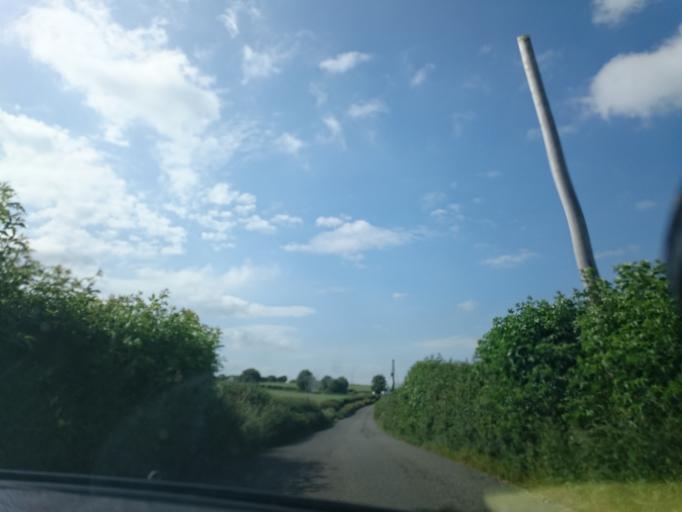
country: IE
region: Leinster
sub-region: Kilkenny
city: Thomastown
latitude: 52.5222
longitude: -7.1983
